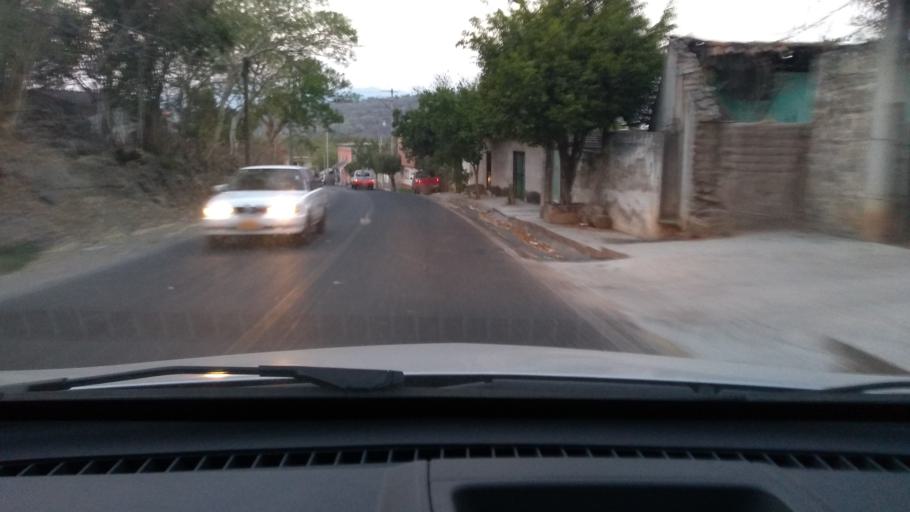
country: MX
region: Morelos
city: Coatetelco
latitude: 18.7245
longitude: -99.3164
